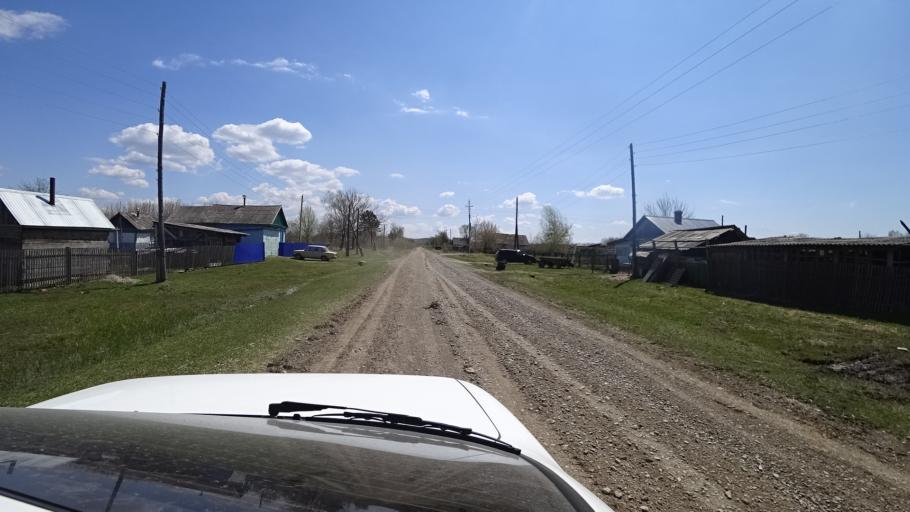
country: RU
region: Primorskiy
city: Lazo
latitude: 45.8014
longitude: 133.7627
